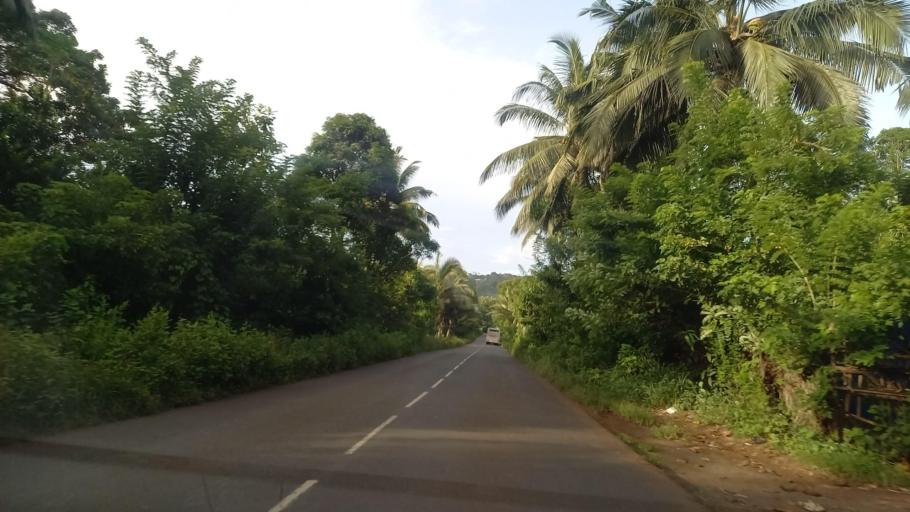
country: YT
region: Bandraboua
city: Bandraboua
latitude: -12.7315
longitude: 45.1196
